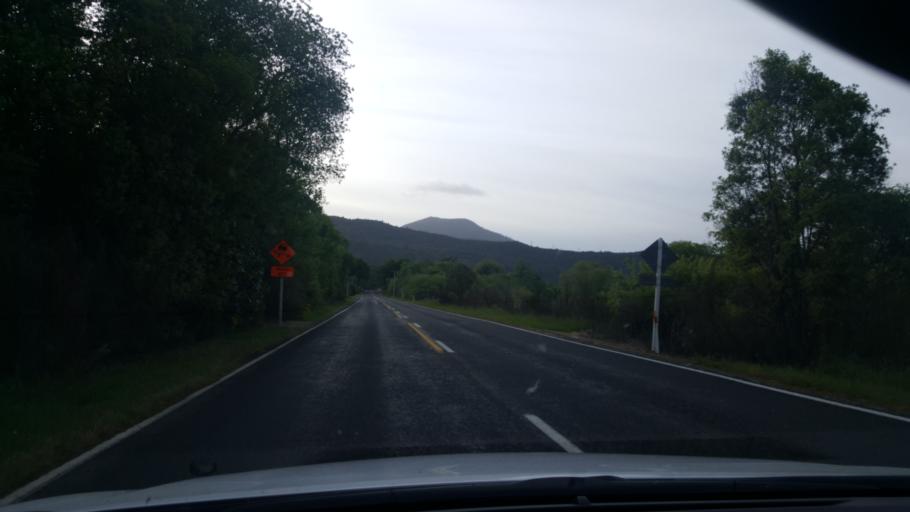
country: NZ
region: Waikato
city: Turangi
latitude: -38.9598
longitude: 175.7622
